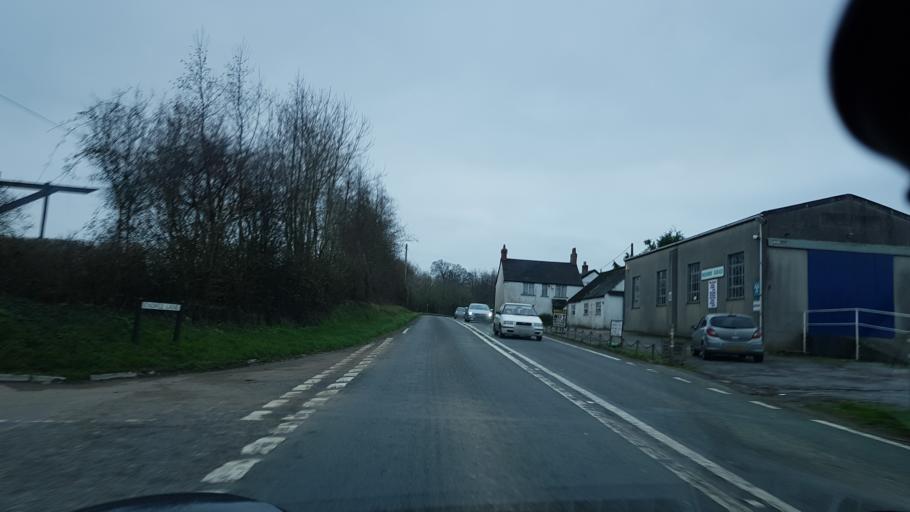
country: GB
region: England
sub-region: Somerset
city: Chard
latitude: 50.8926
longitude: -2.9485
